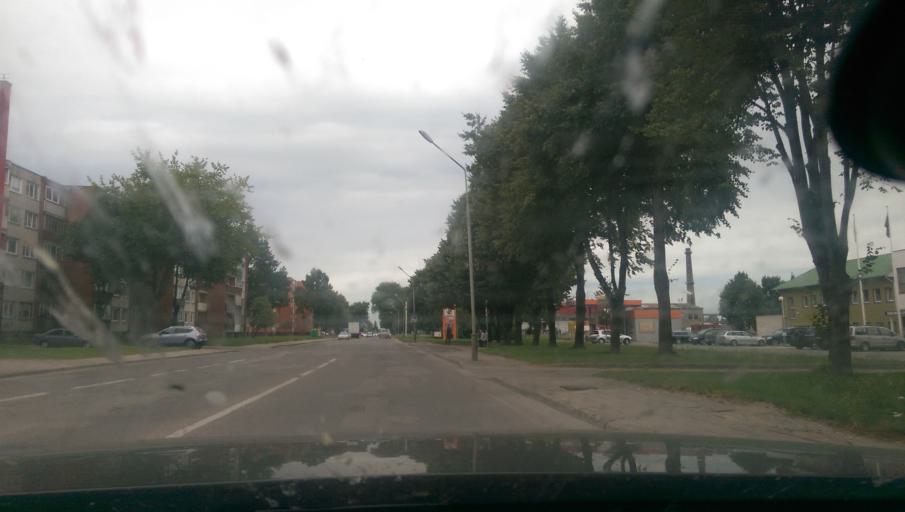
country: LT
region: Klaipedos apskritis
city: Silute
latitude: 55.3480
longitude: 21.4700
